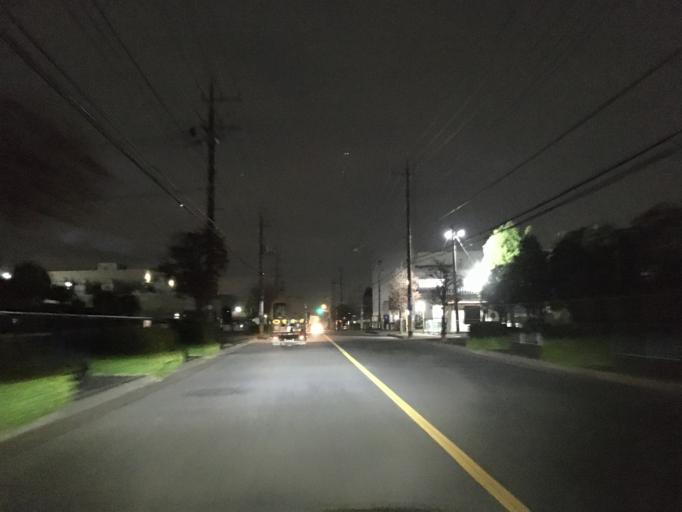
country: JP
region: Saitama
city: Sayama
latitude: 35.8711
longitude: 139.3937
